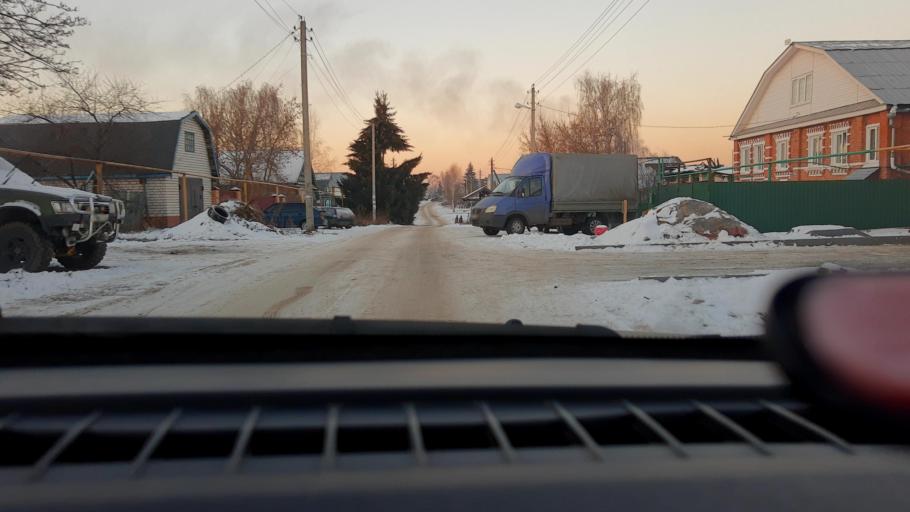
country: RU
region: Nizjnij Novgorod
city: Afonino
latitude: 56.2181
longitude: 44.1147
